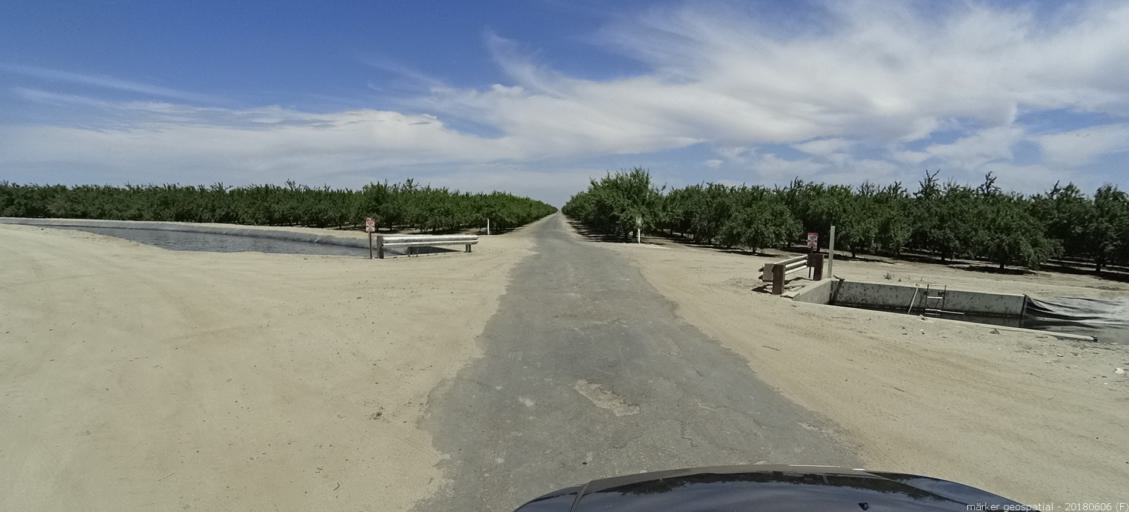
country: US
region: California
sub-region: Fresno County
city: Firebaugh
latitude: 36.8701
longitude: -120.3999
